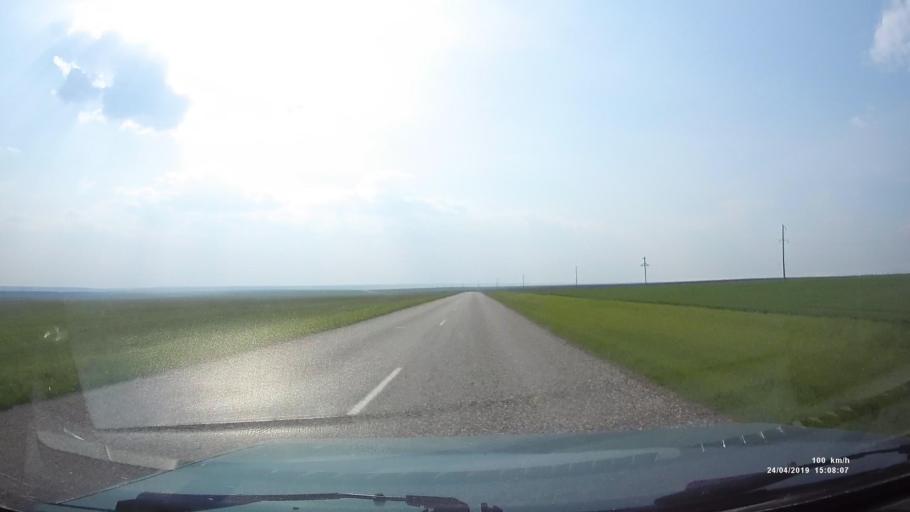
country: RU
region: Rostov
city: Remontnoye
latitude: 46.5600
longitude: 43.3902
